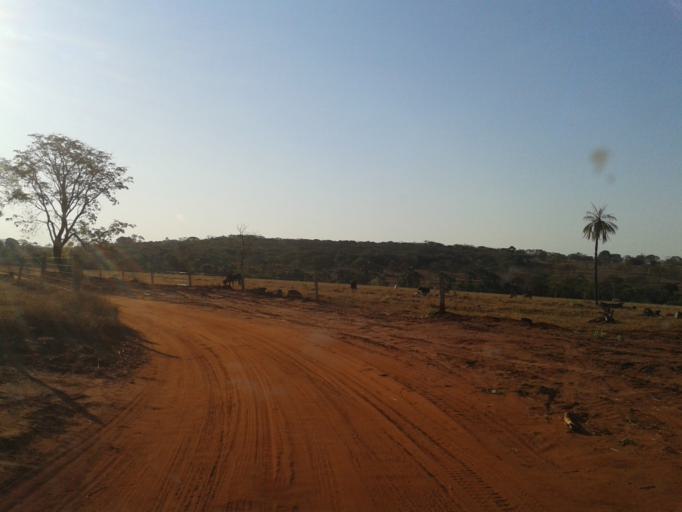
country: BR
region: Minas Gerais
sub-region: Ituiutaba
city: Ituiutaba
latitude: -19.2489
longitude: -49.5785
